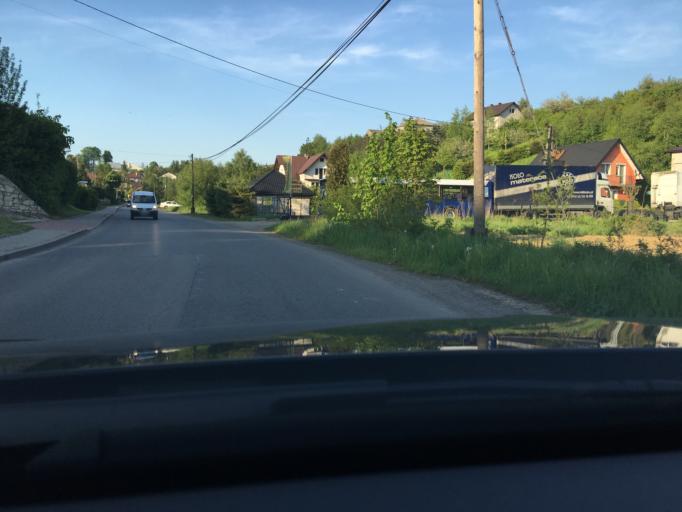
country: PL
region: Lesser Poland Voivodeship
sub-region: Powiat krakowski
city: Jerzmanowice
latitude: 50.2066
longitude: 19.7409
